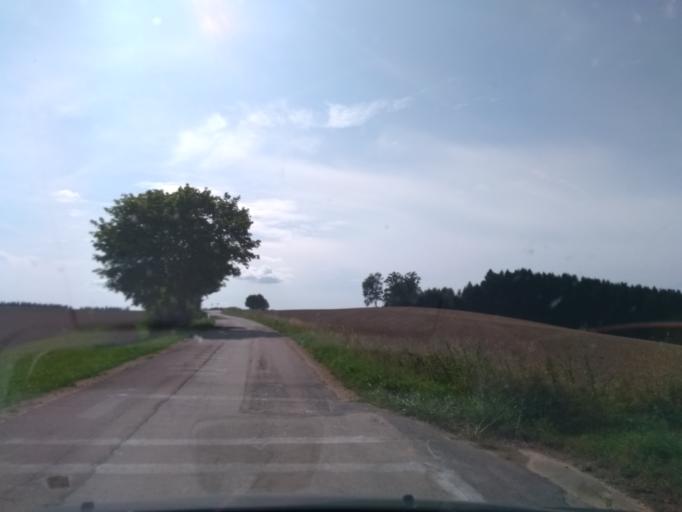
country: DE
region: Bavaria
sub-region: Upper Bavaria
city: Schwabhausen
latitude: 48.4010
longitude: 11.3541
